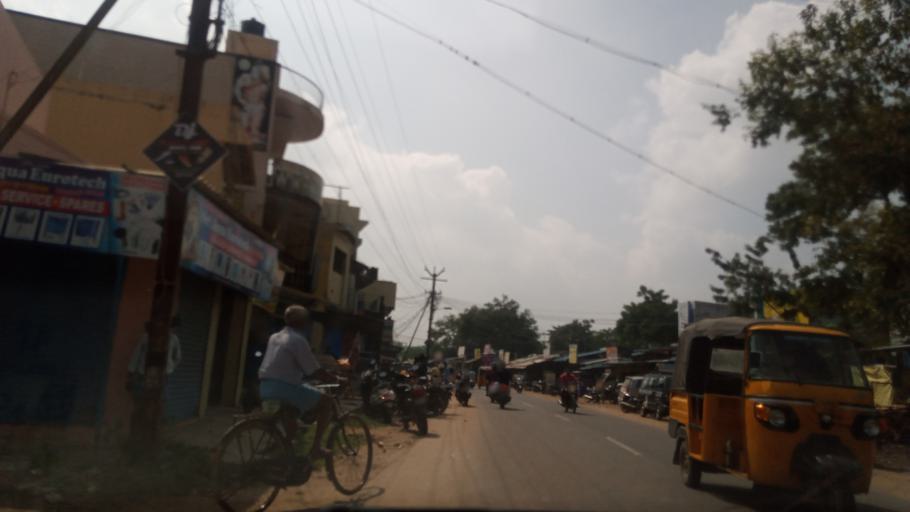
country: IN
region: Tamil Nadu
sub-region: Vellore
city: Arakkonam
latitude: 13.0768
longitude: 79.6712
